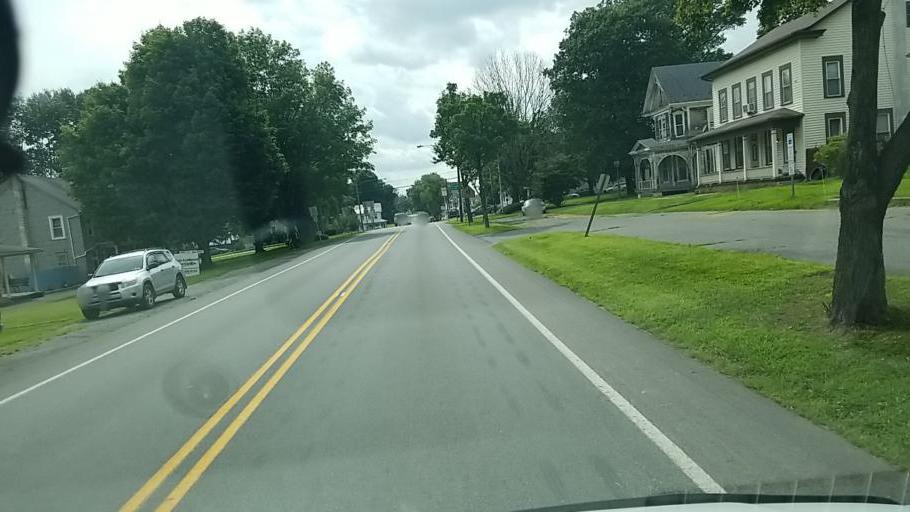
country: US
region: Pennsylvania
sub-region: Dauphin County
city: Elizabethville
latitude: 40.6023
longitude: -76.8108
